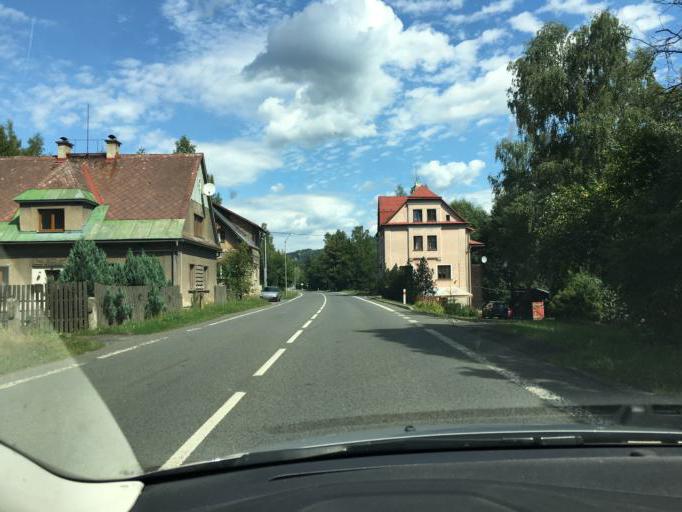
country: CZ
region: Liberecky
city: Velke Hamry
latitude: 50.7095
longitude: 15.3163
